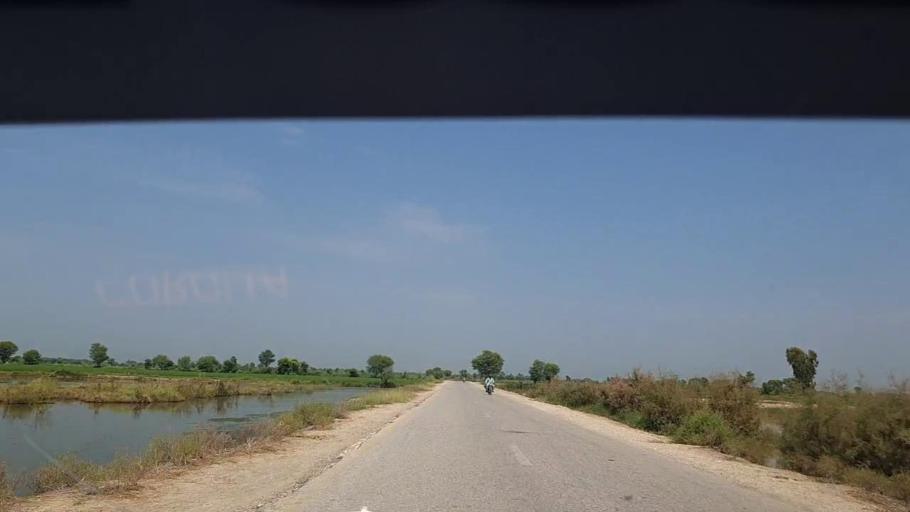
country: PK
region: Sindh
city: Thul
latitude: 28.1296
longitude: 68.8178
